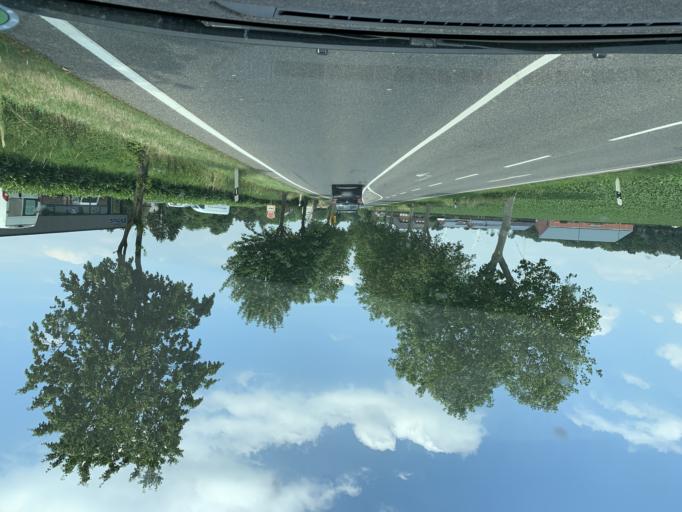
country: DE
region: North Rhine-Westphalia
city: Neu-Pattern
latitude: 50.8934
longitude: 6.2750
